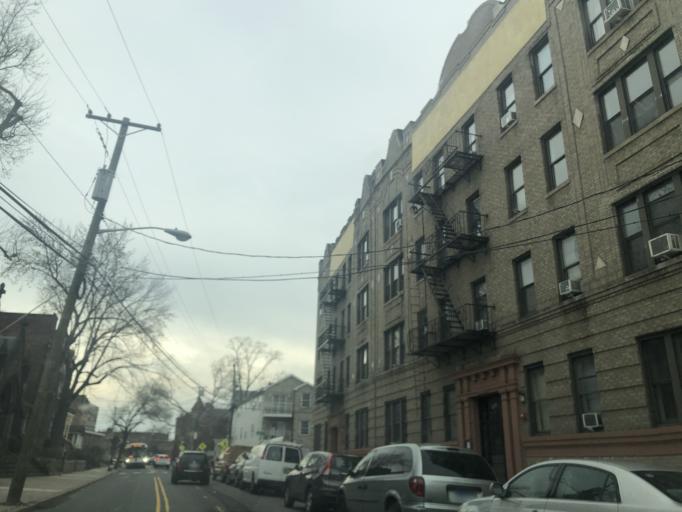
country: US
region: New Jersey
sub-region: Hudson County
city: Jersey City
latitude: 40.7199
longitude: -74.0671
